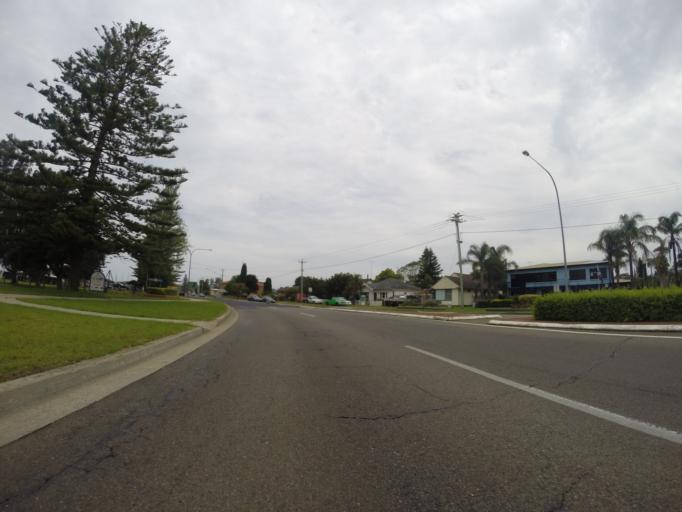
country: AU
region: New South Wales
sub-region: Eurobodalla
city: Batemans Bay
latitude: -35.7128
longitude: 150.1858
